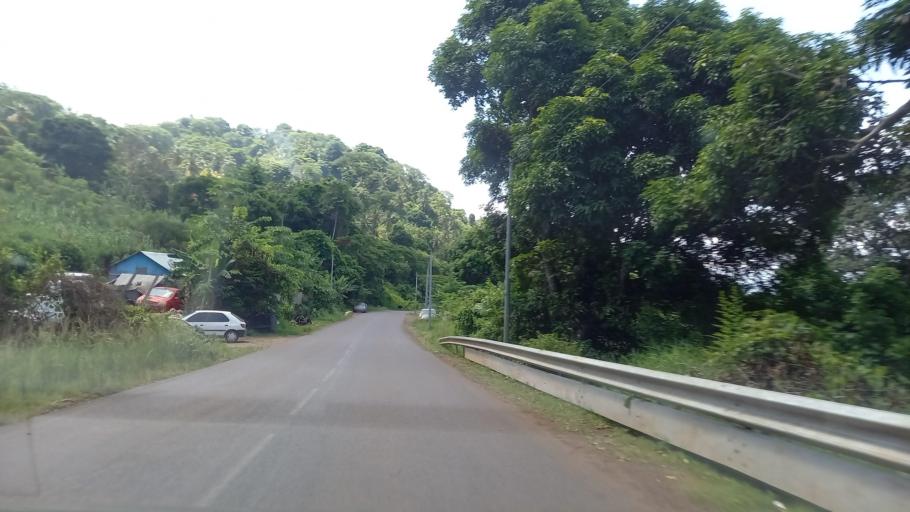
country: YT
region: M'Tsangamouji
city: M'Tsangamouji
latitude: -12.7560
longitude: 45.0895
